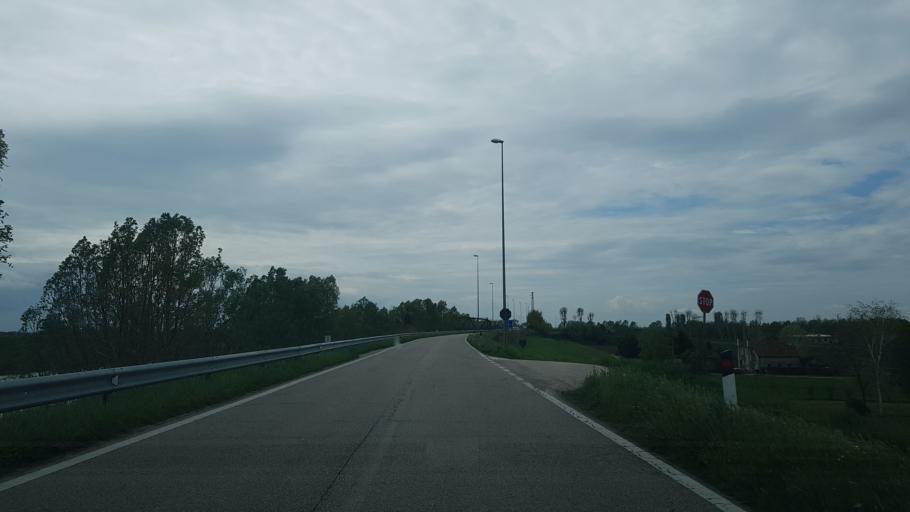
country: IT
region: Veneto
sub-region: Provincia di Rovigo
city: Lendinara
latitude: 45.1102
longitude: 11.6229
